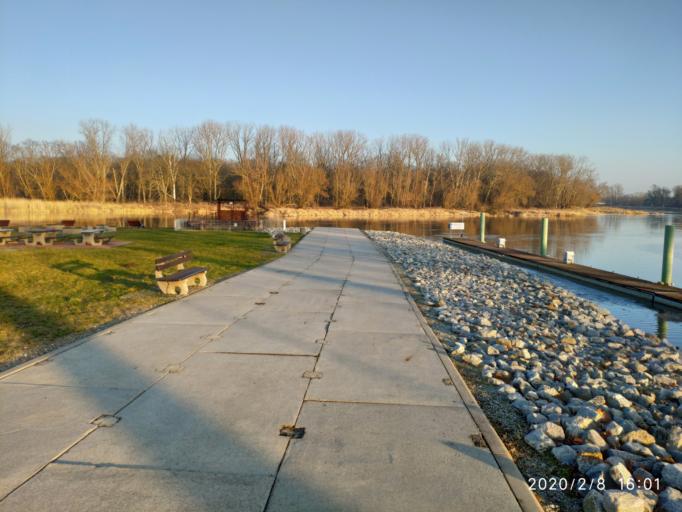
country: PL
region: Lubusz
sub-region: Powiat nowosolski
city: Nowa Sol
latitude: 51.8031
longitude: 15.7255
